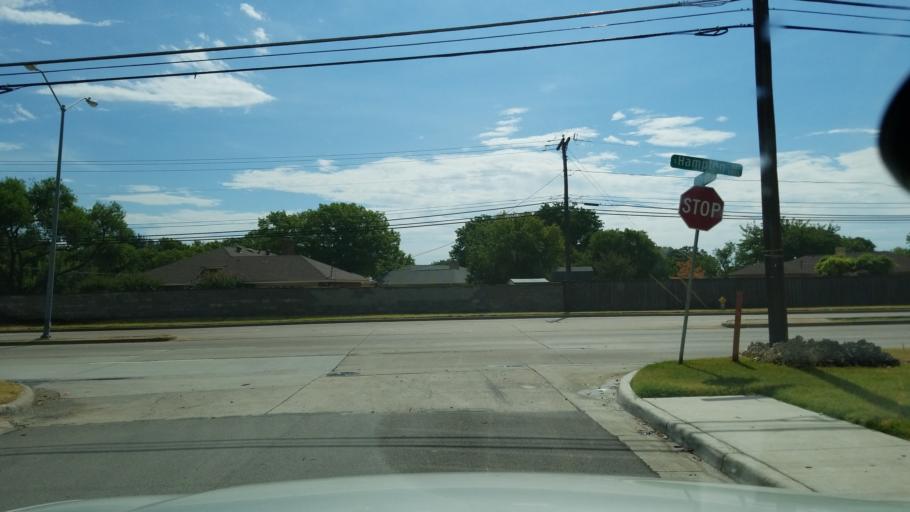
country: US
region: Texas
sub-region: Dallas County
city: Duncanville
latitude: 32.6692
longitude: -96.8574
